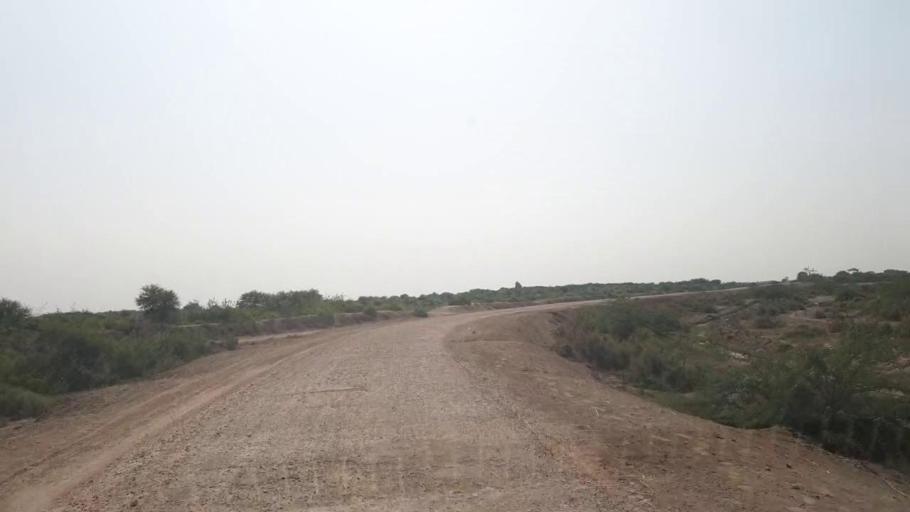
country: PK
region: Sindh
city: Kadhan
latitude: 24.4645
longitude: 68.9059
